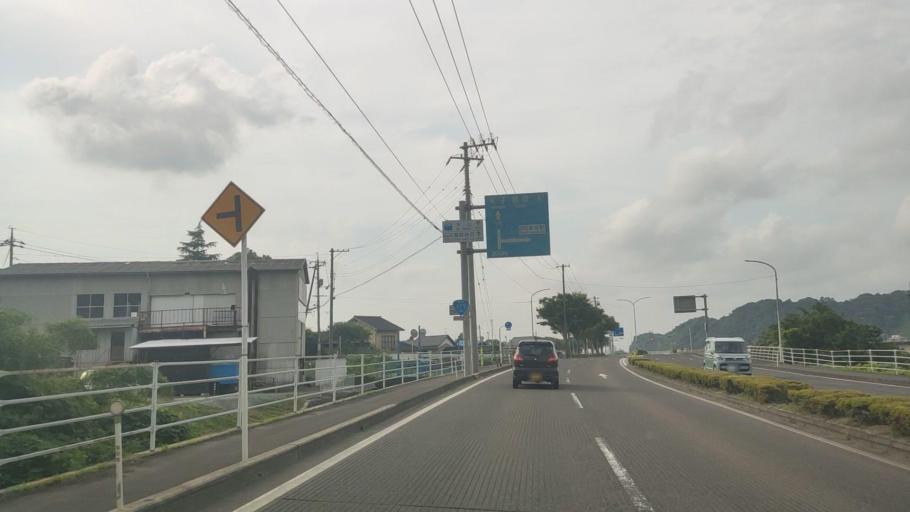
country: JP
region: Tottori
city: Kurayoshi
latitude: 35.4212
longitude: 133.8495
